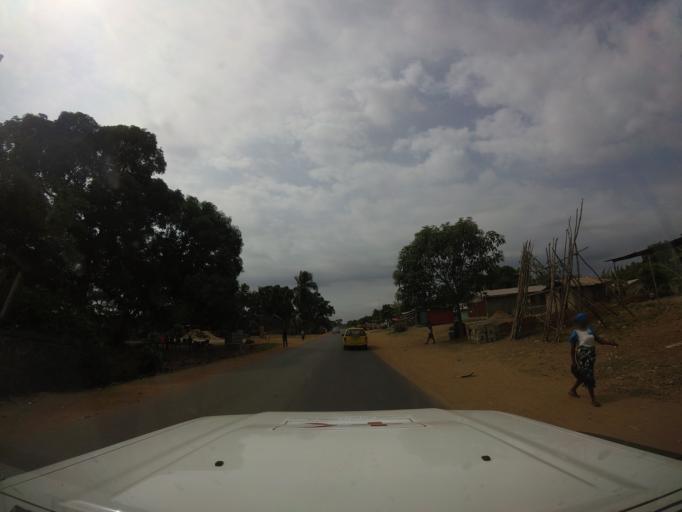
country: LR
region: Montserrado
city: Monrovia
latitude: 6.4468
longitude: -10.7998
